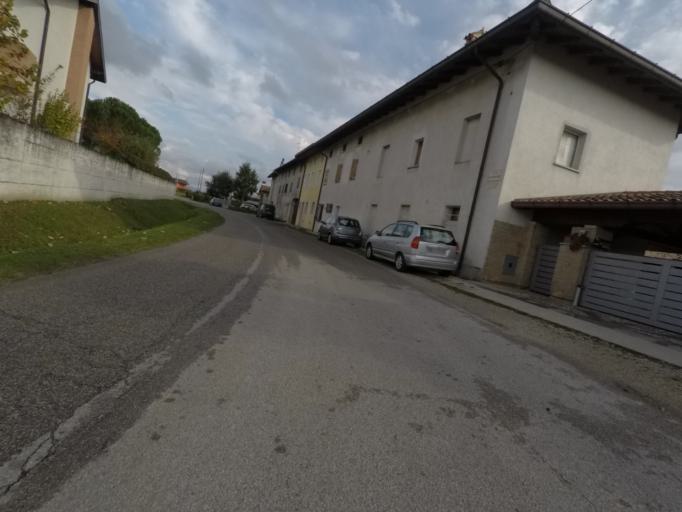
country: IT
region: Friuli Venezia Giulia
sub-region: Provincia di Udine
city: Udine
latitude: 46.0416
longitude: 13.2611
